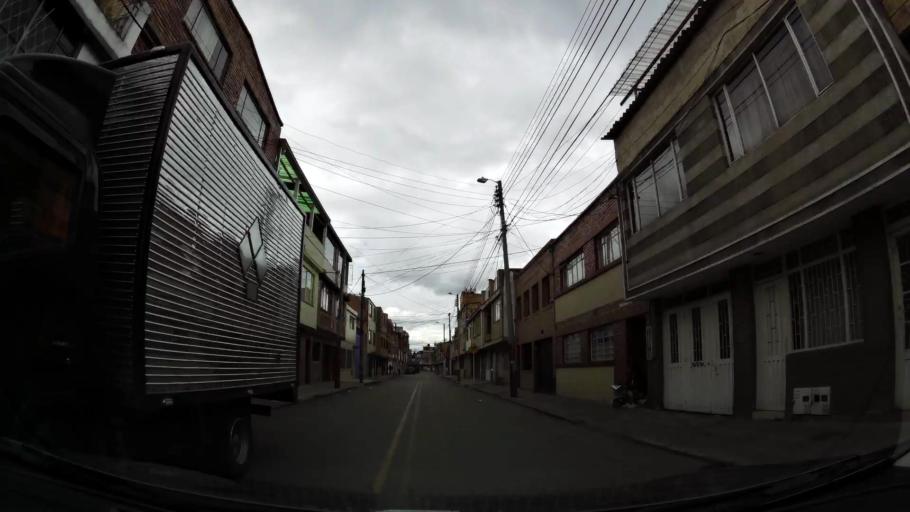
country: CO
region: Bogota D.C.
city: Bogota
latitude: 4.6786
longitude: -74.0940
